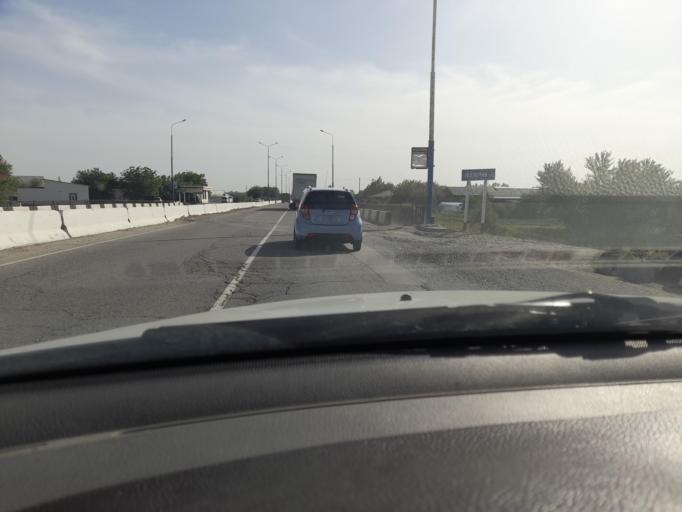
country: UZ
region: Samarqand
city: Kattaqo'rg'on
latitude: 39.9262
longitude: 66.3583
